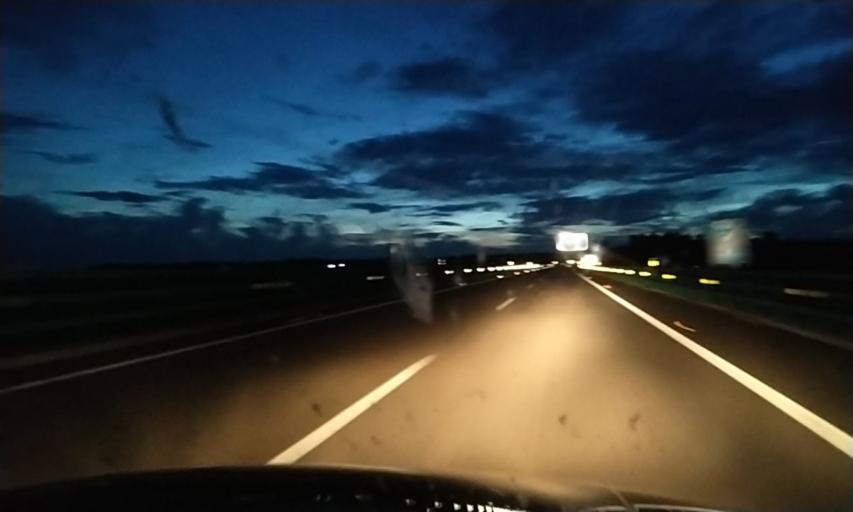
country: ES
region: Extremadura
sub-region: Provincia de Caceres
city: Galisteo
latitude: 39.9843
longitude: -6.2622
